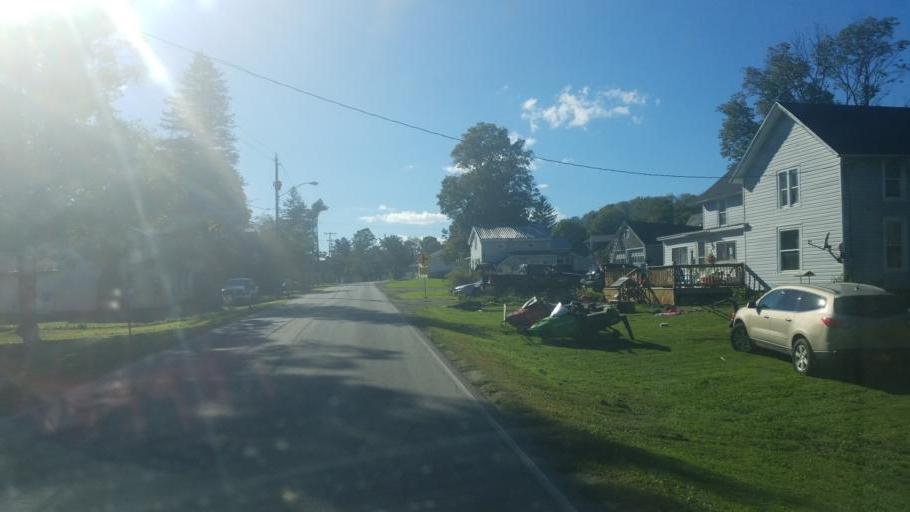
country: US
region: New York
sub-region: Allegany County
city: Cuba
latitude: 42.2756
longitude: -78.2242
